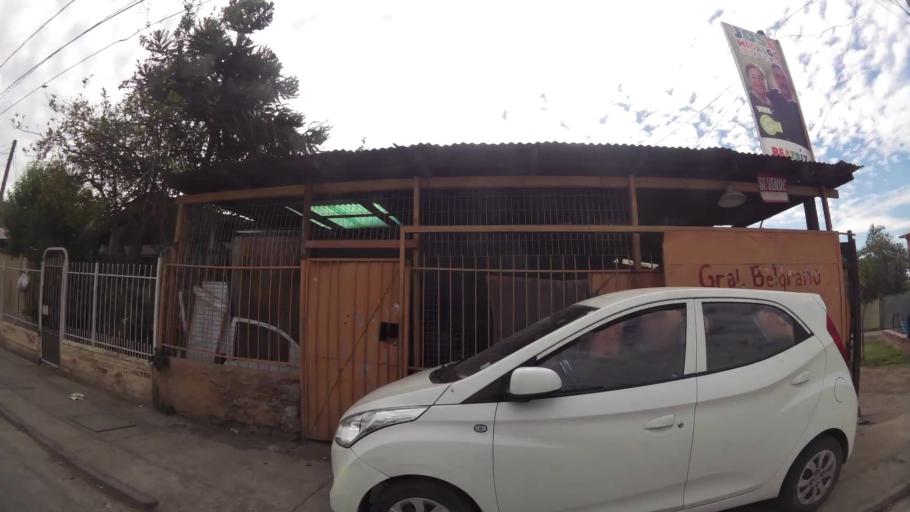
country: CL
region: Santiago Metropolitan
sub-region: Provincia de Santiago
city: La Pintana
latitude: -33.5799
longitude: -70.6365
